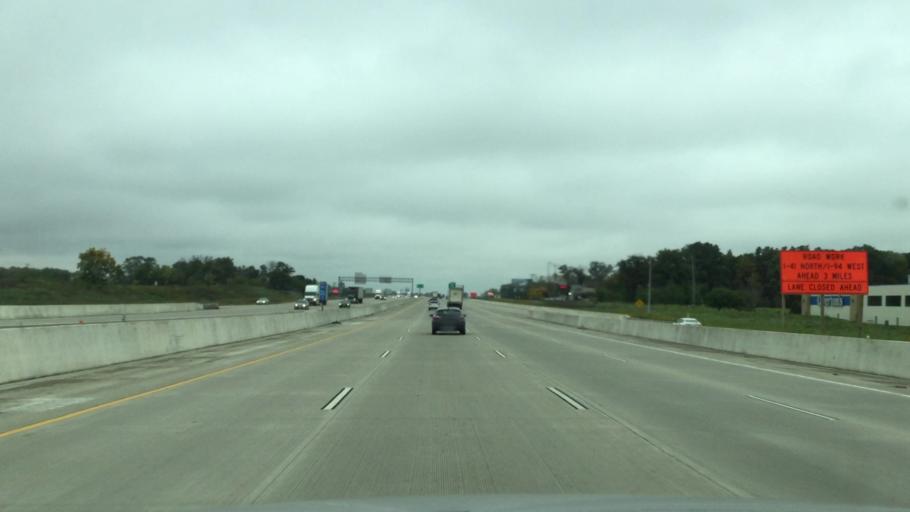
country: US
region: Wisconsin
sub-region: Kenosha County
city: Pleasant Prairie
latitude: 42.5728
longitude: -87.9527
